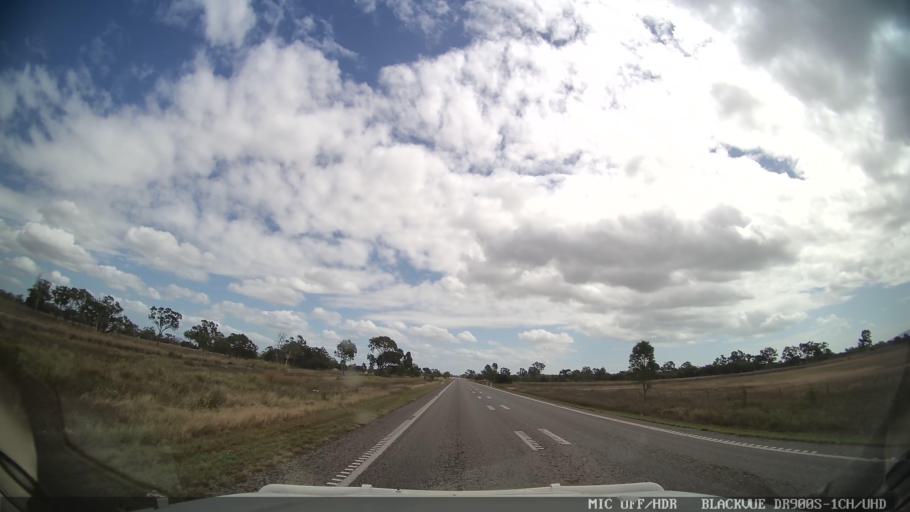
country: AU
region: Queensland
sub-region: Burdekin
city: Home Hill
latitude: -19.9070
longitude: 147.7736
